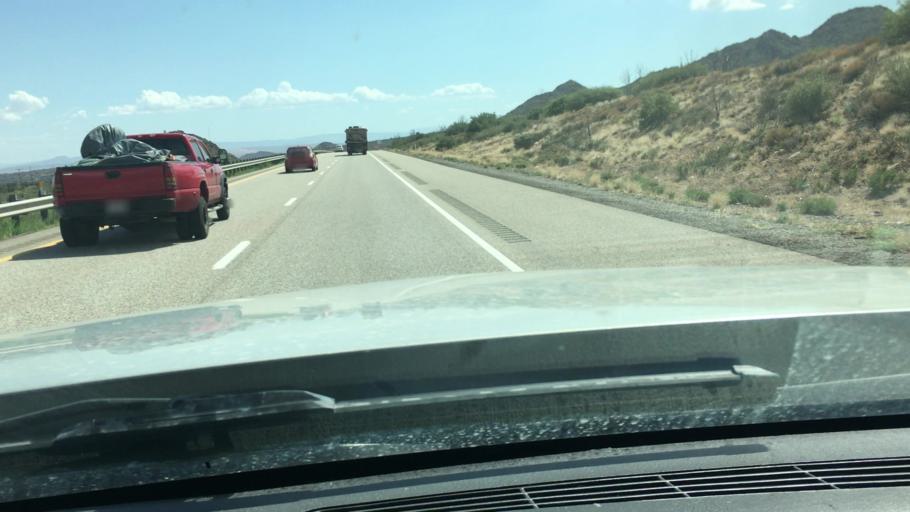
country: US
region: Utah
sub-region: Washington County
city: Toquerville
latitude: 37.3190
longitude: -113.2906
